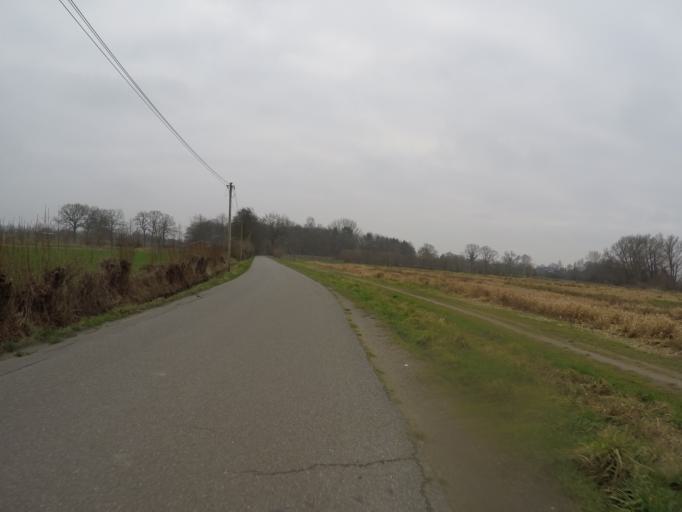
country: DE
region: Schleswig-Holstein
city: Tangstedt
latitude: 53.6912
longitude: 9.8542
